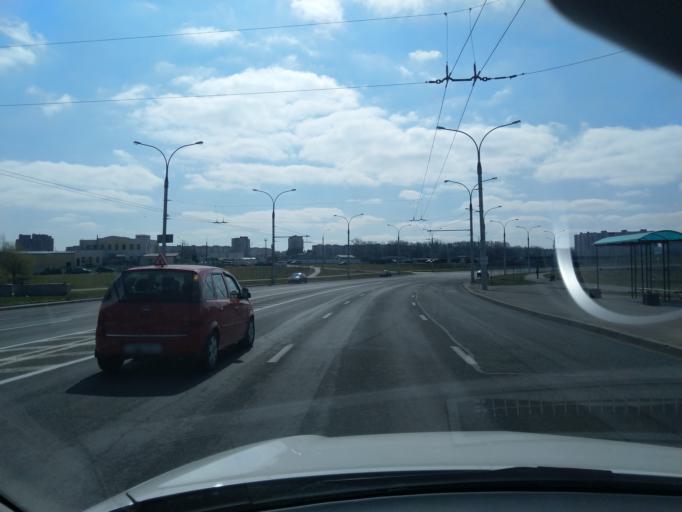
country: BY
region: Minsk
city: Syenitsa
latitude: 53.8574
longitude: 27.4980
